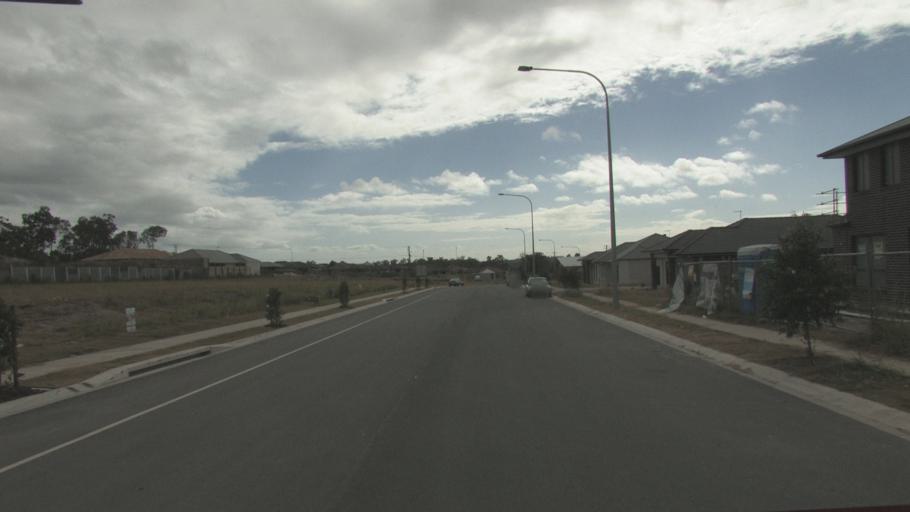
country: AU
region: Queensland
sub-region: Logan
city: Park Ridge South
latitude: -27.6912
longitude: 153.0484
